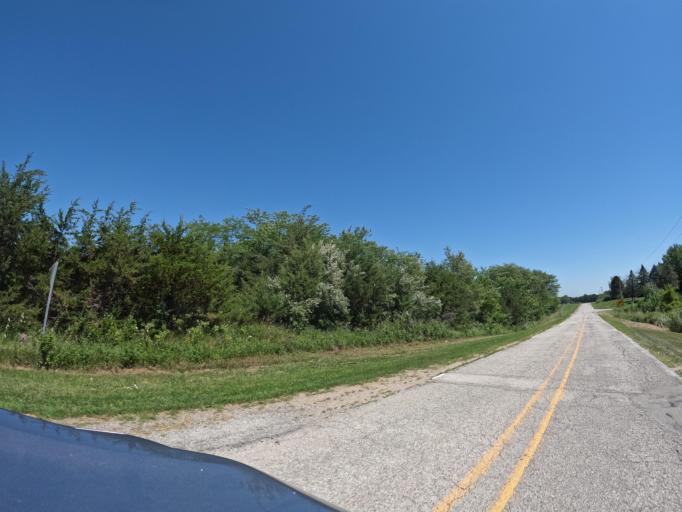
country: US
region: Iowa
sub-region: Monroe County
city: Albia
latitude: 41.0285
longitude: -92.7702
